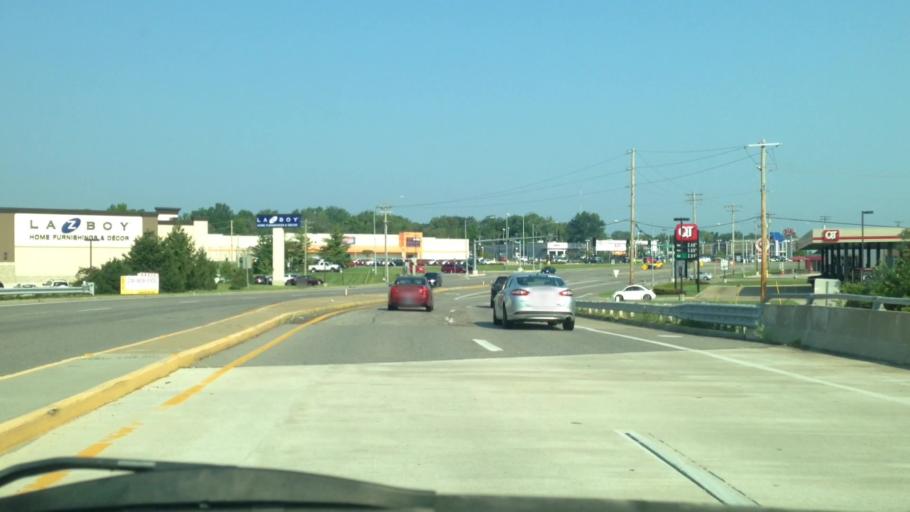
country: US
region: Missouri
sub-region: Saint Louis County
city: Green Park
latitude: 38.5137
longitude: -90.3410
